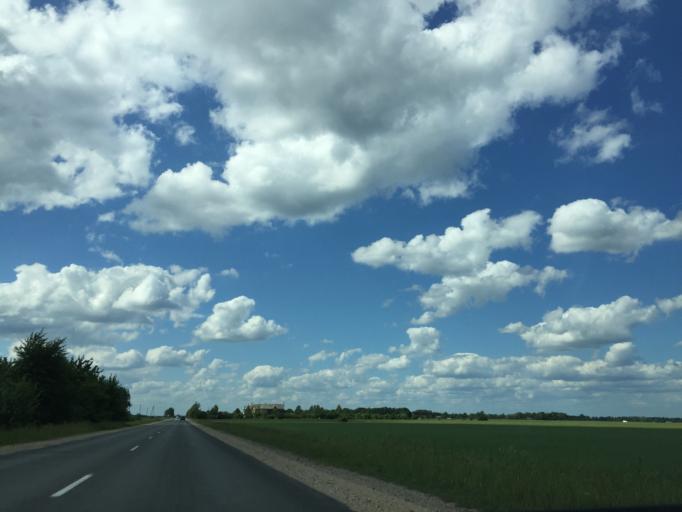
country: LV
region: Tukuma Rajons
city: Tukums
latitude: 56.9094
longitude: 23.2259
